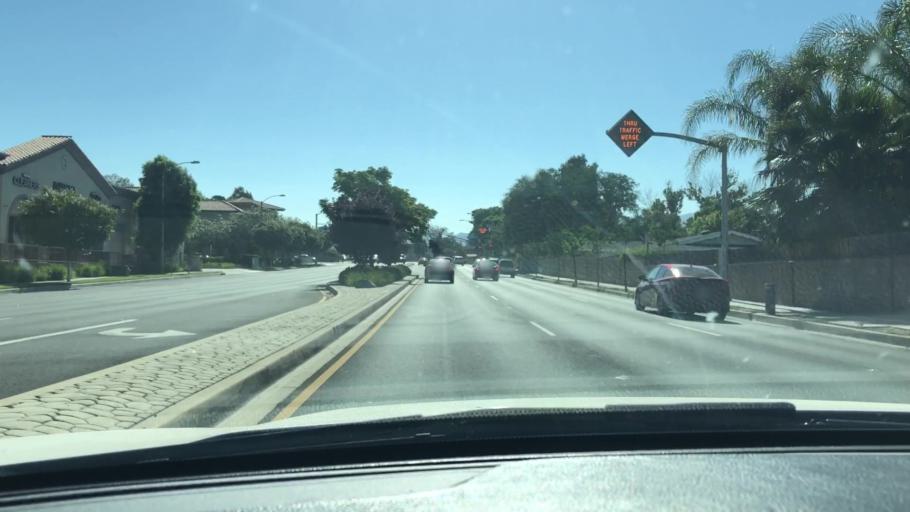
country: US
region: California
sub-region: Los Angeles County
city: Santa Clarita
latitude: 34.4159
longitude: -118.4605
